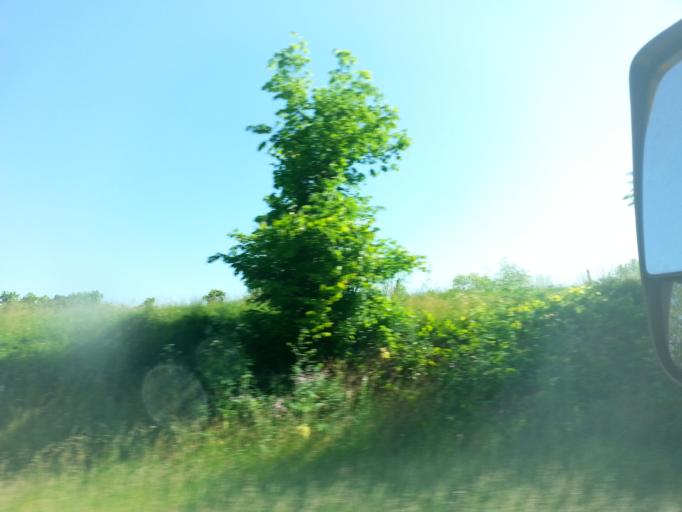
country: US
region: Kentucky
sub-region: Shelby County
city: Shelbyville
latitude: 38.1834
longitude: -85.1902
